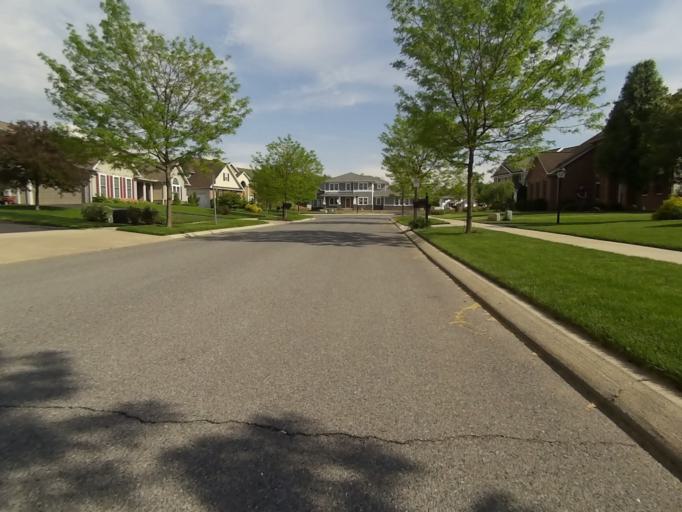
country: US
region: Pennsylvania
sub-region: Centre County
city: Houserville
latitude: 40.8313
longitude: -77.8236
